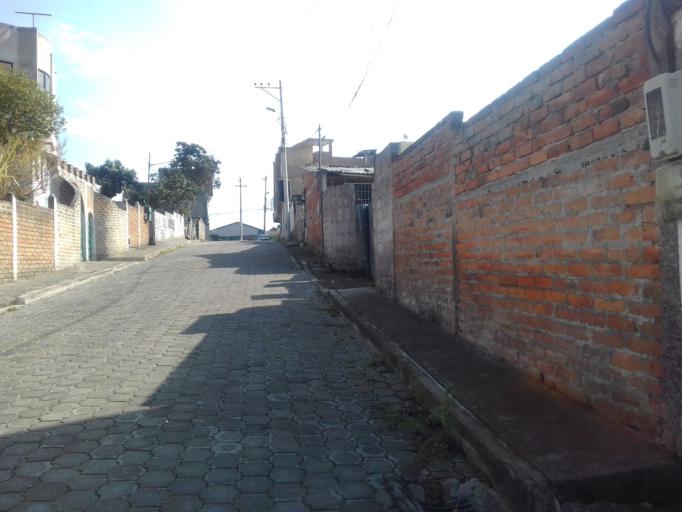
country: EC
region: Pichincha
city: Sangolqui
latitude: -0.3300
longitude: -78.4290
